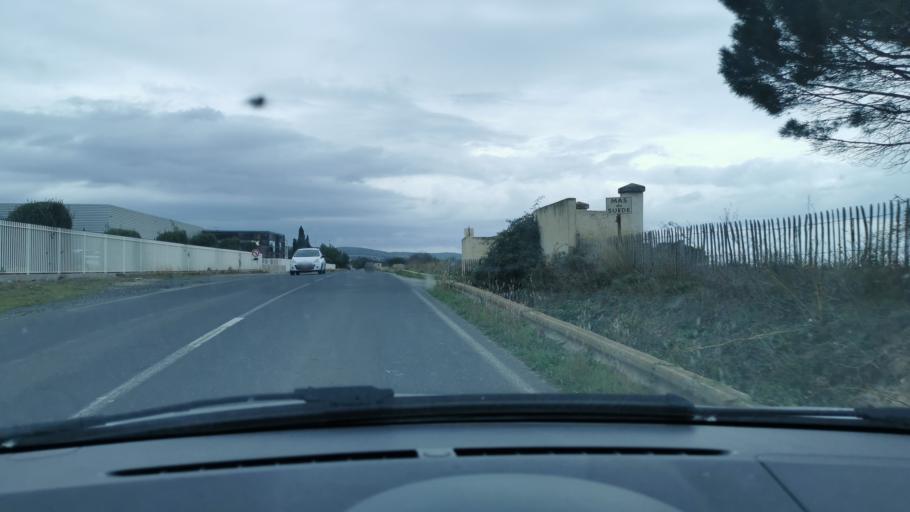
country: FR
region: Languedoc-Roussillon
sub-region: Departement de l'Herault
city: Balaruc-les-Bains
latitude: 43.4371
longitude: 3.7090
